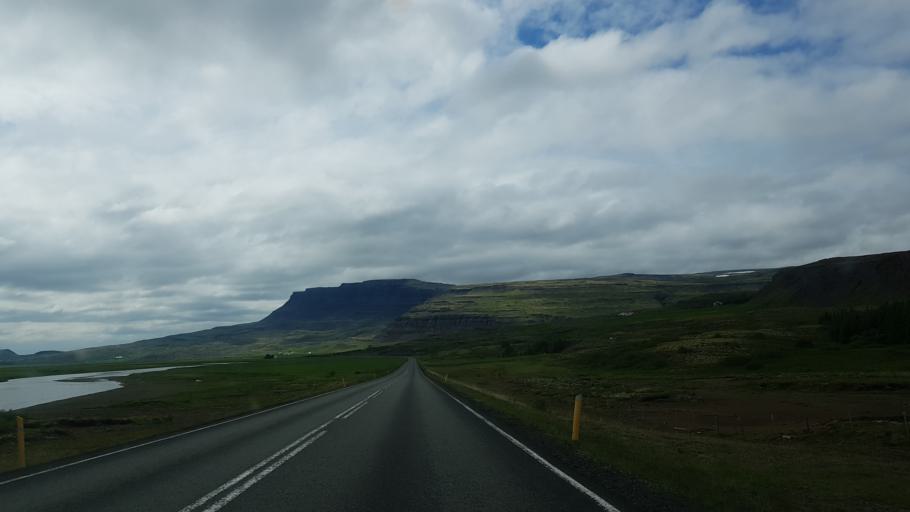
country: IS
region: West
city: Borgarnes
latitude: 64.8049
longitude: -21.4369
